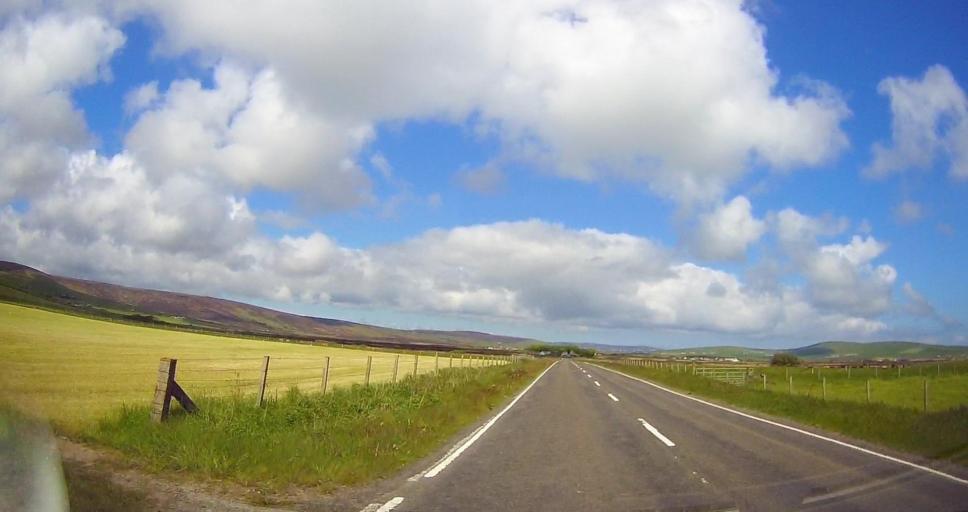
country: GB
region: Scotland
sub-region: Orkney Islands
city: Orkney
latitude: 59.0382
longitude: -3.0878
